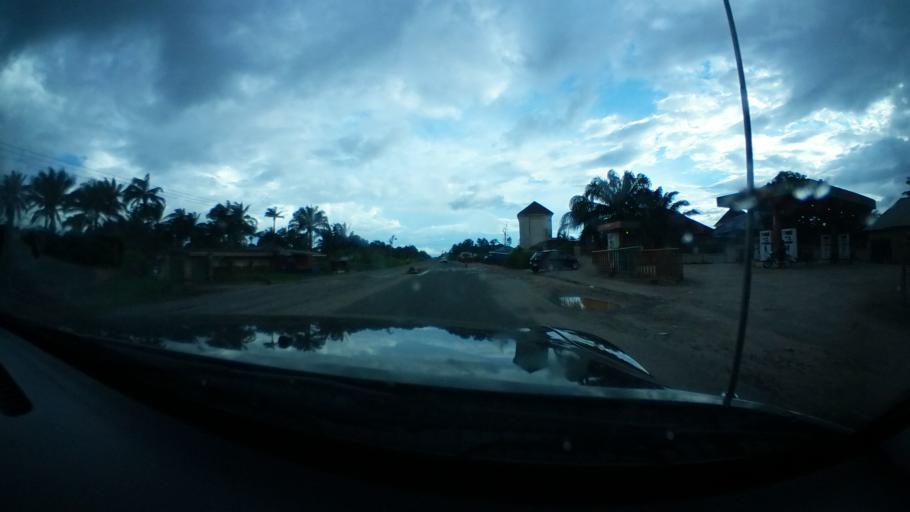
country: NG
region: Imo
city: Orlu
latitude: 5.7878
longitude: 7.0162
